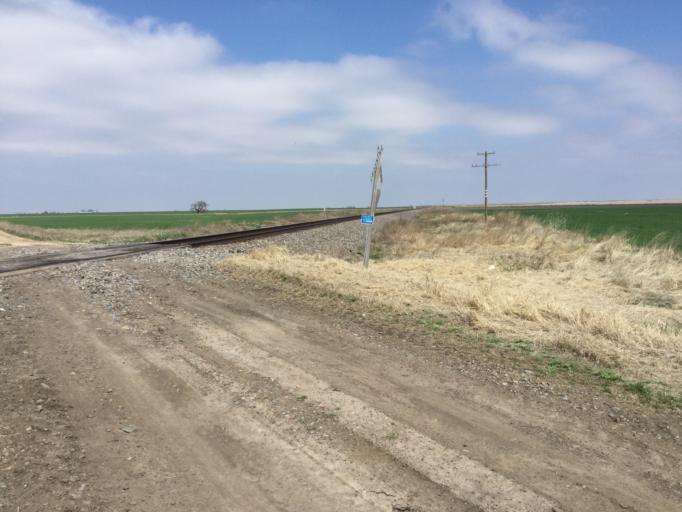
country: US
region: Kansas
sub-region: Russell County
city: Russell
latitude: 38.8674
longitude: -98.7437
